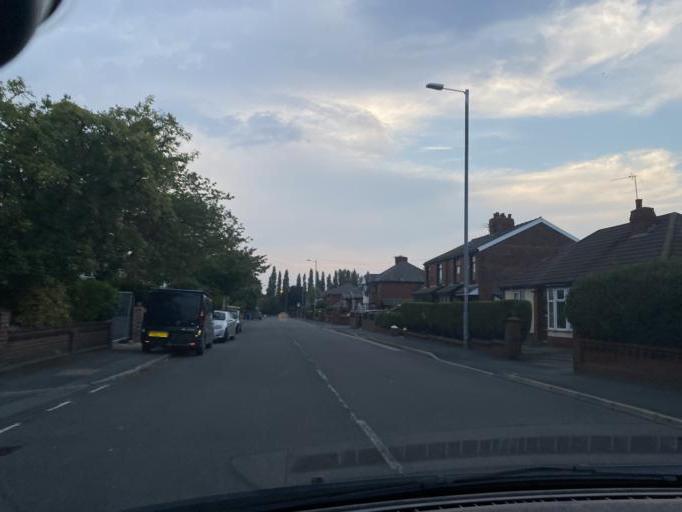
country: GB
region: England
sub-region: Borough of Tameside
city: Denton
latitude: 53.4703
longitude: -2.1229
